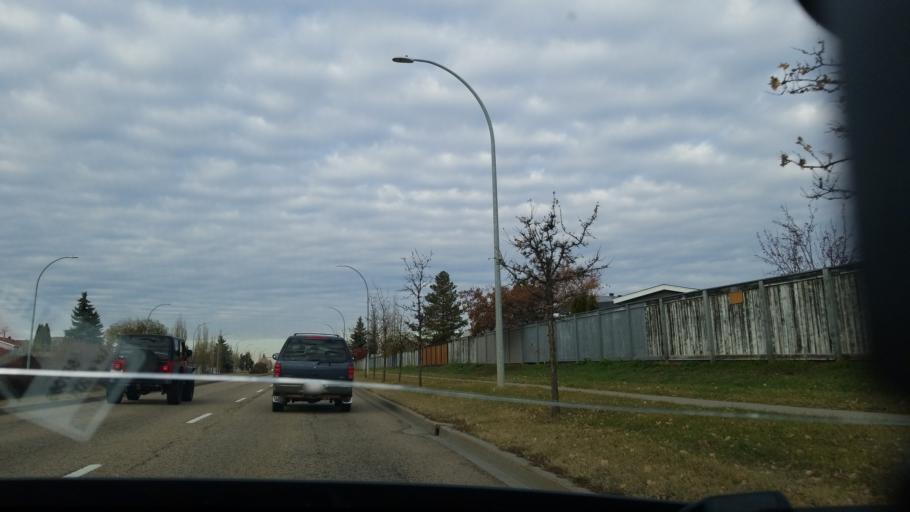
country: CA
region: Alberta
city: Edmonton
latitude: 53.6160
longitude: -113.4617
